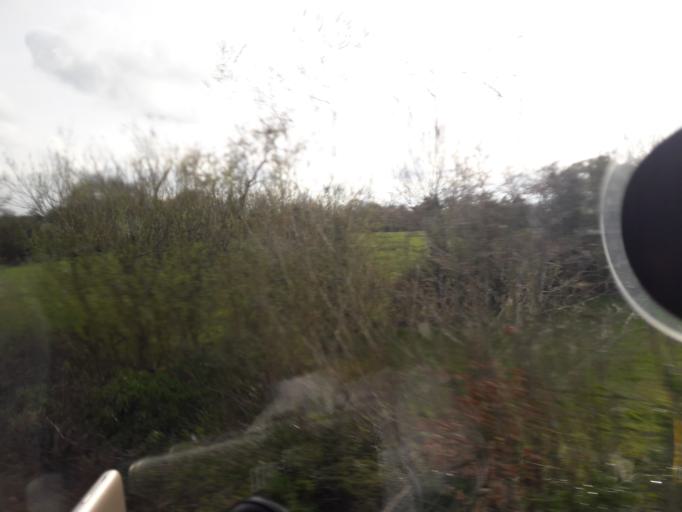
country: IE
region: Leinster
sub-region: An Mhi
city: Longwood
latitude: 53.4590
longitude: -6.9647
